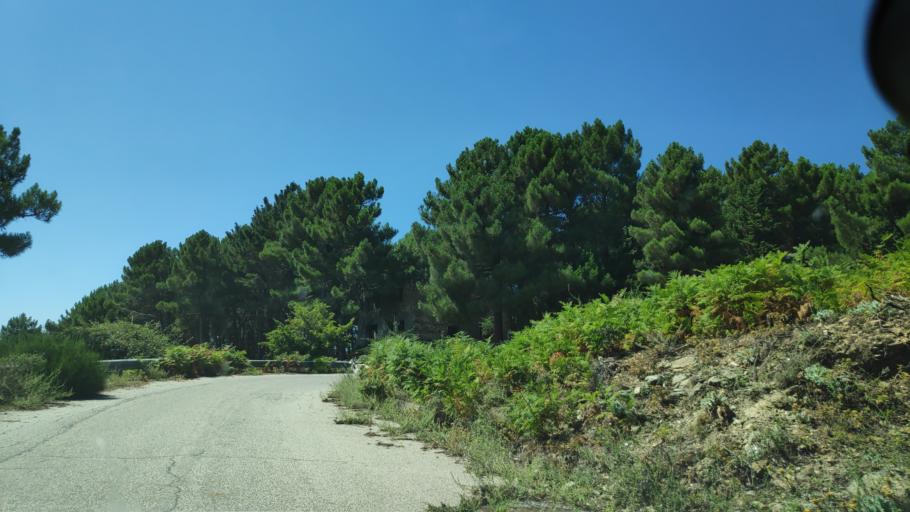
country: IT
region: Calabria
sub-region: Provincia di Reggio Calabria
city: Bova
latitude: 38.0267
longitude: 15.9414
